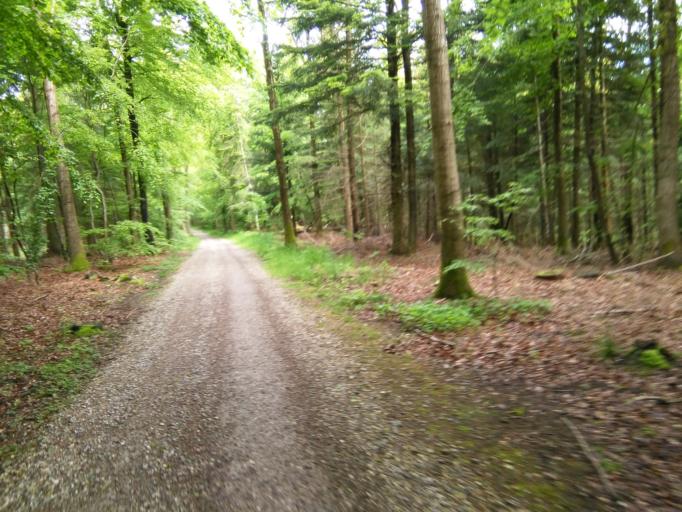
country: DK
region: Central Jutland
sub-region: Arhus Kommune
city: Beder
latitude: 56.0696
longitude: 10.2431
